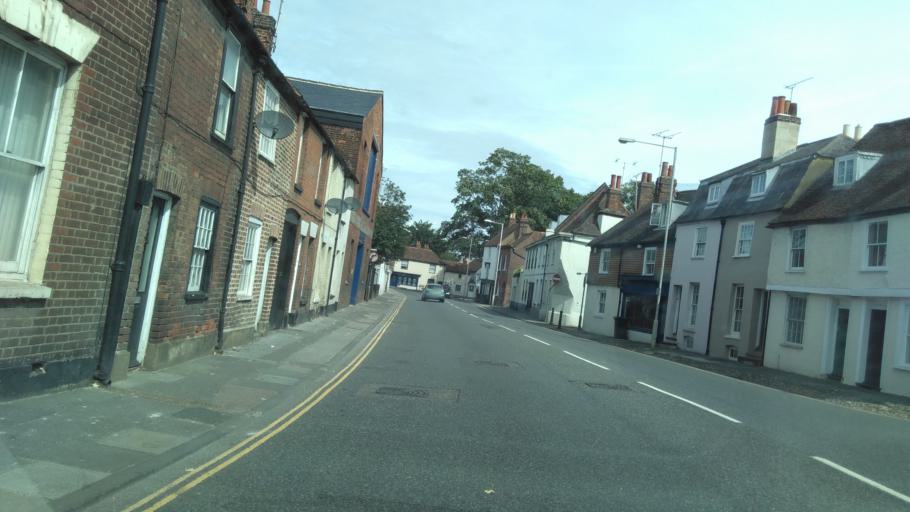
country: GB
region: England
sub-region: Kent
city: Canterbury
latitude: 51.2801
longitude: 1.0860
